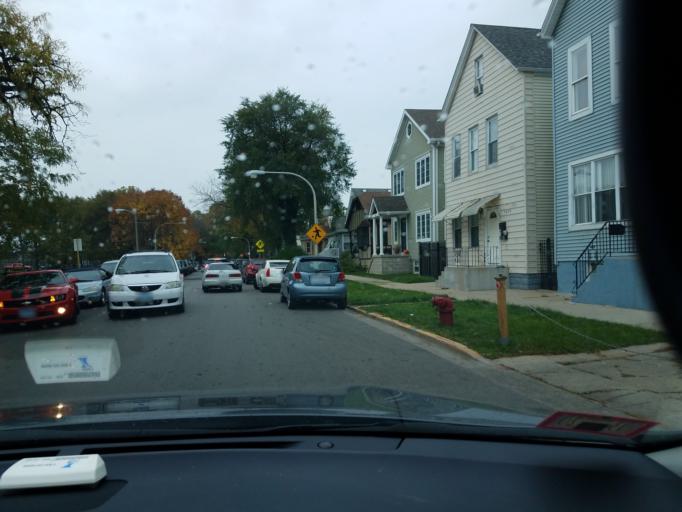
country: US
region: Illinois
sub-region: Cook County
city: Lincolnwood
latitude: 41.9454
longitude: -87.7397
